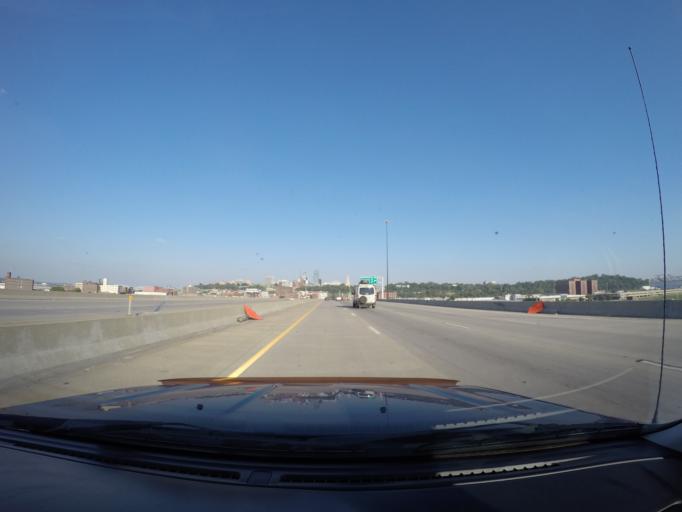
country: US
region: Kansas
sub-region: Wyandotte County
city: Kansas City
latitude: 39.0988
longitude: -94.6106
